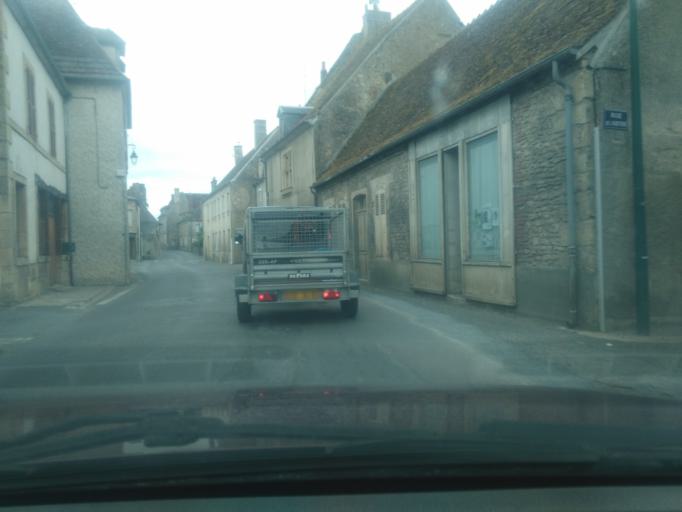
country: FR
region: Centre
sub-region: Departement du Cher
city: Charenton-du-Cher
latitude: 46.7296
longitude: 2.6415
